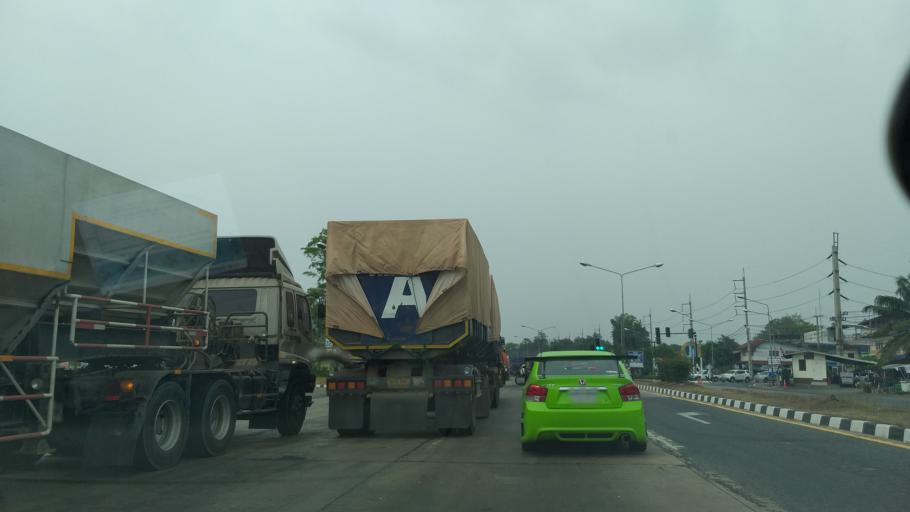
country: TH
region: Chon Buri
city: Ko Chan
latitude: 13.3240
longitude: 101.2700
